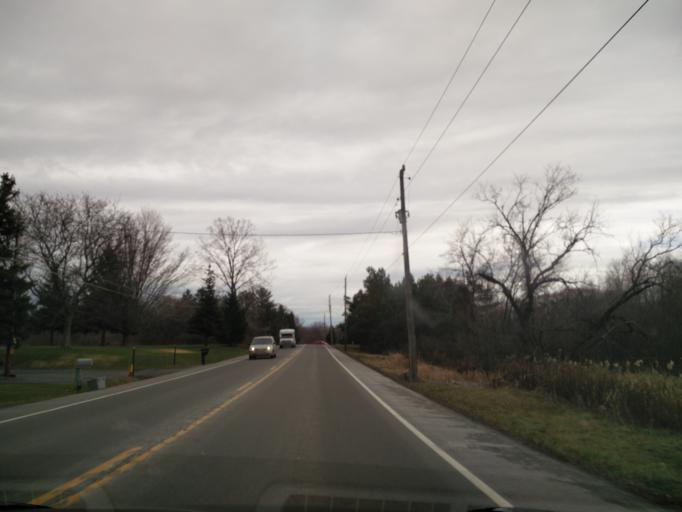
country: US
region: New York
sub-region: Tompkins County
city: Northwest Ithaca
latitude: 42.4827
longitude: -76.5657
